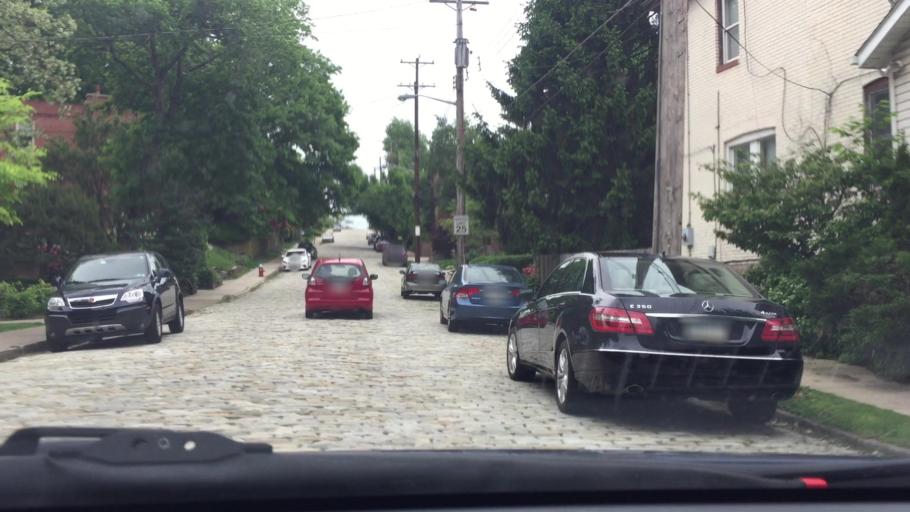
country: US
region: Pennsylvania
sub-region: Allegheny County
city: Bloomfield
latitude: 40.4355
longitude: -79.9307
